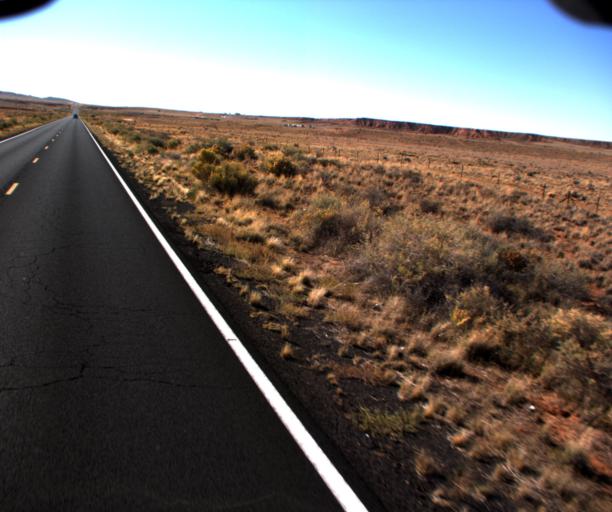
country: US
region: Arizona
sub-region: Navajo County
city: Dilkon
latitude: 35.3388
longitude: -110.4238
